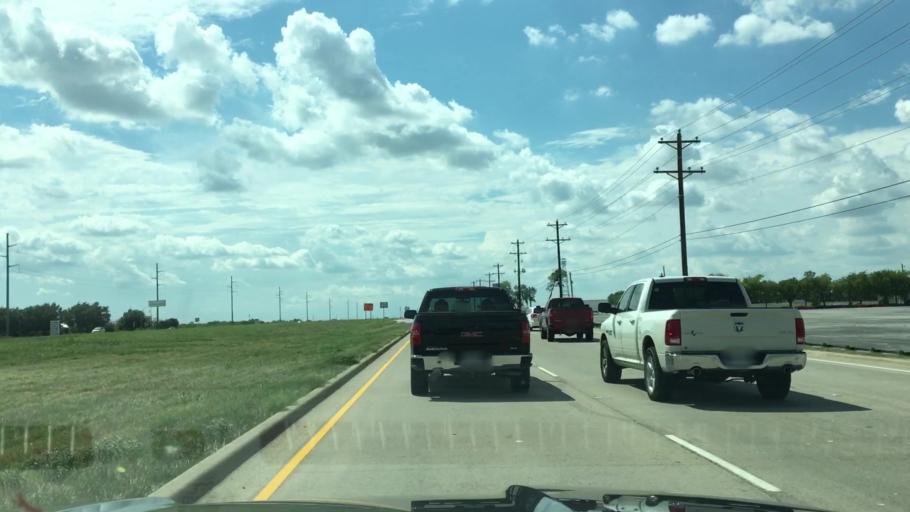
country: US
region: Texas
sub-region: Denton County
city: Justin
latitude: 33.0270
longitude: -97.2850
